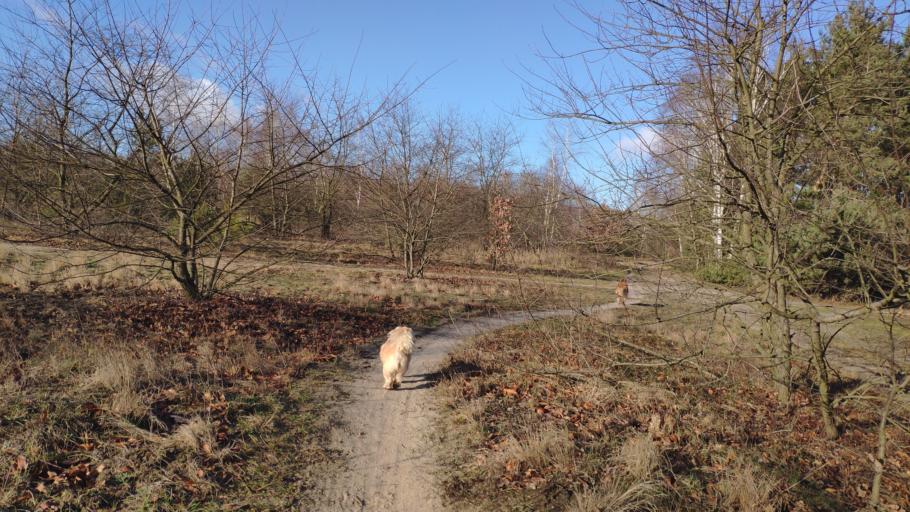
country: PL
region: Lodz Voivodeship
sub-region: Powiat pabianicki
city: Ksawerow
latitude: 51.7280
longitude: 19.4115
